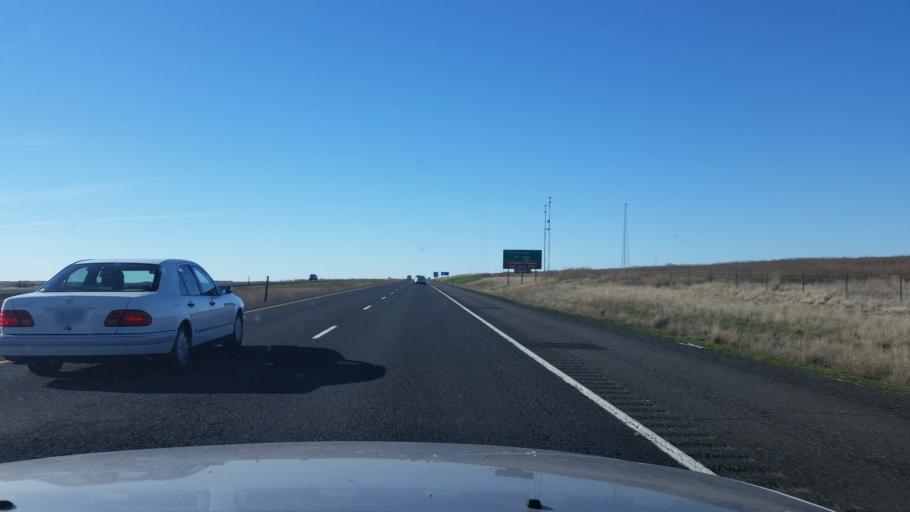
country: US
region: Washington
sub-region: Spokane County
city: Medical Lake
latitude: 47.3221
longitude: -117.9432
